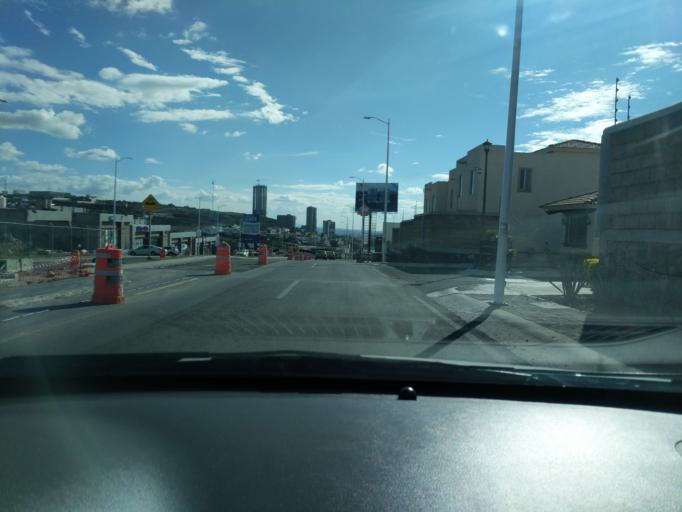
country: MX
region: Queretaro
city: La Canada
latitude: 20.5905
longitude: -100.3360
